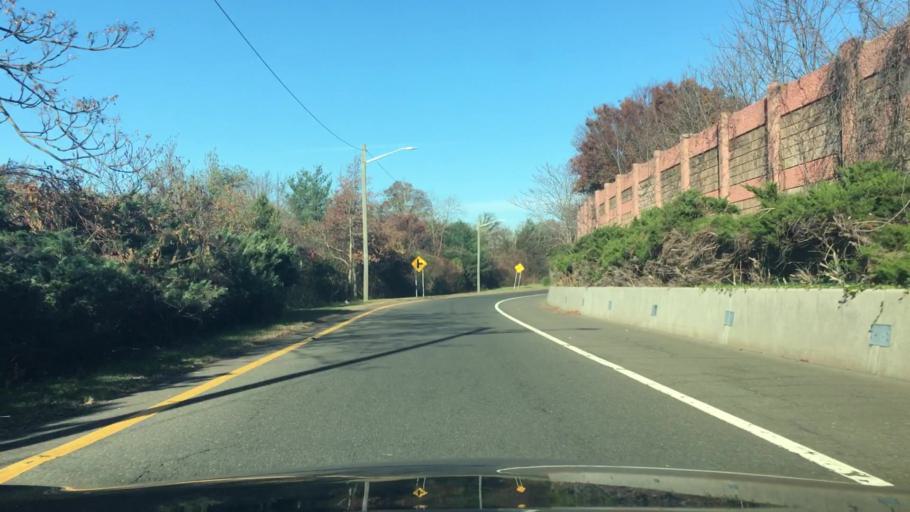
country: US
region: New York
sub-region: Nassau County
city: Syosset
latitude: 40.8014
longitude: -73.4880
